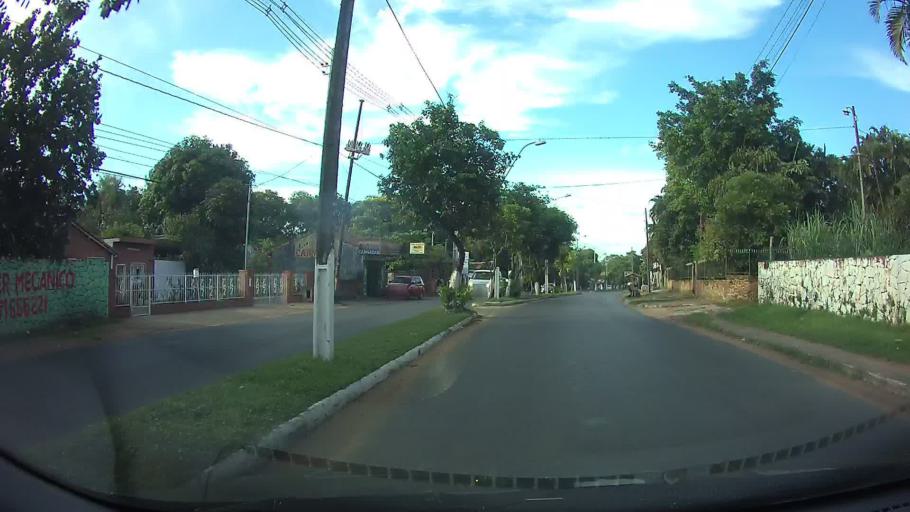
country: PY
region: Central
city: San Antonio
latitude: -25.4106
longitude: -57.5740
